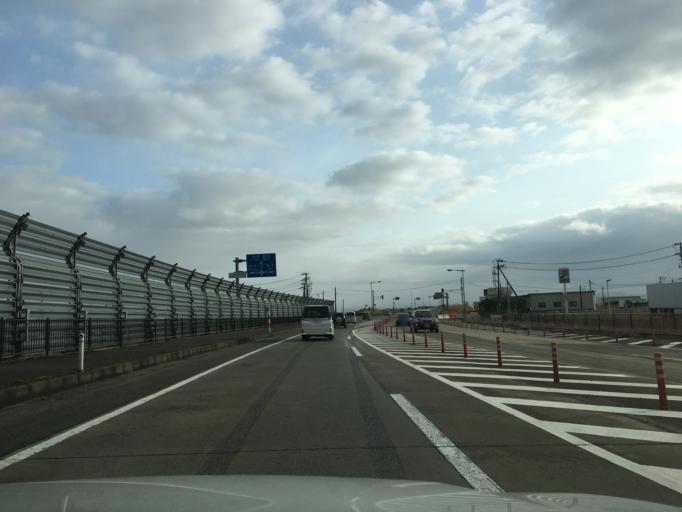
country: JP
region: Yamagata
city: Sakata
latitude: 38.8224
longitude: 139.8345
